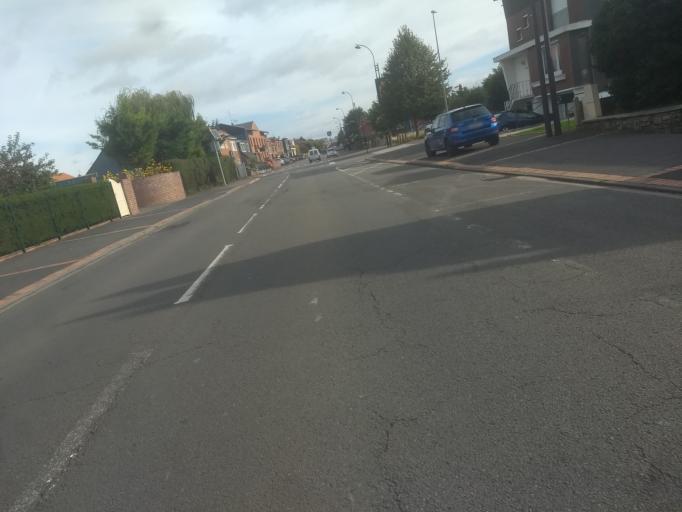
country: FR
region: Nord-Pas-de-Calais
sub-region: Departement du Pas-de-Calais
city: Dainville
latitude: 50.2843
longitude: 2.7367
